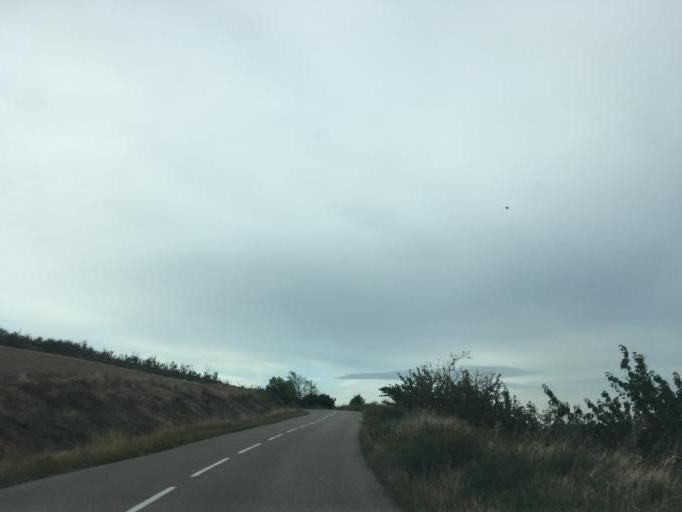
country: FR
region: Rhone-Alpes
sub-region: Departement de la Loire
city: Saint-Martin-la-Plaine
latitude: 45.5377
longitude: 4.5984
